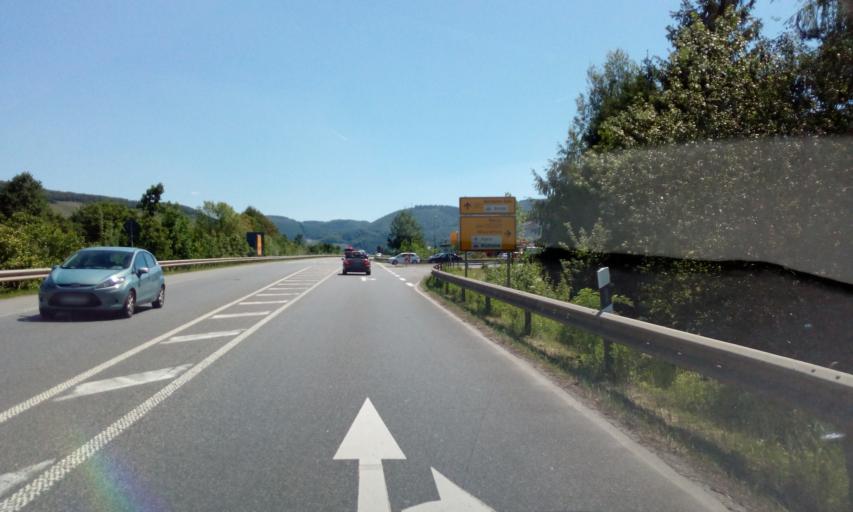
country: DE
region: Rheinland-Pfalz
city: Lieser
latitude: 49.9140
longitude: 7.0169
